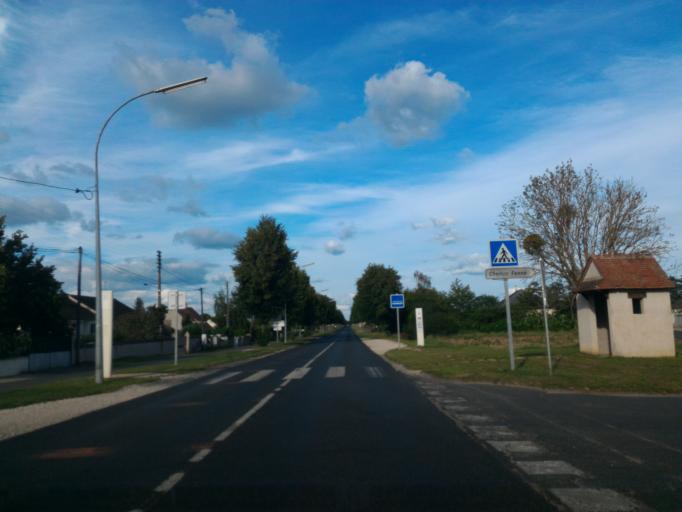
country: FR
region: Centre
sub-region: Departement du Loir-et-Cher
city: Saint-Dye-sur-Loire
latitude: 47.6577
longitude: 1.4968
